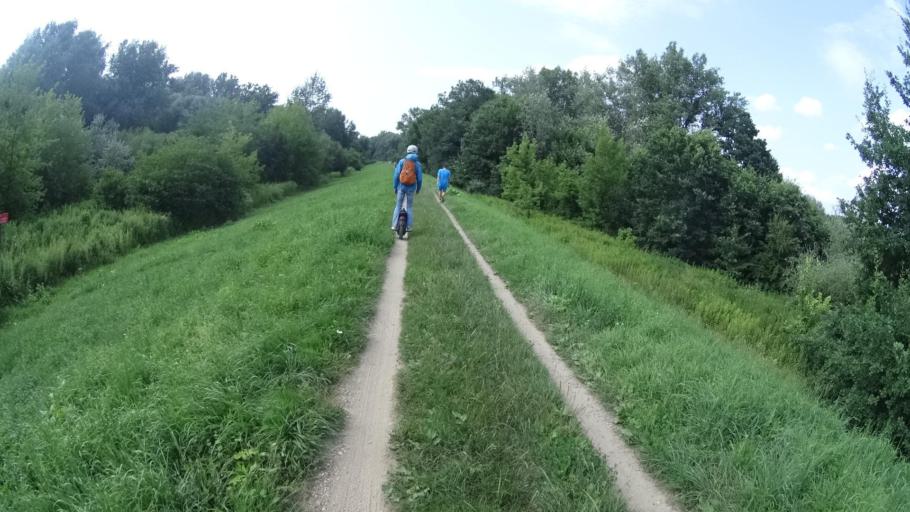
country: PL
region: Masovian Voivodeship
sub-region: Powiat legionowski
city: Jablonna
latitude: 52.3682
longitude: 20.9165
